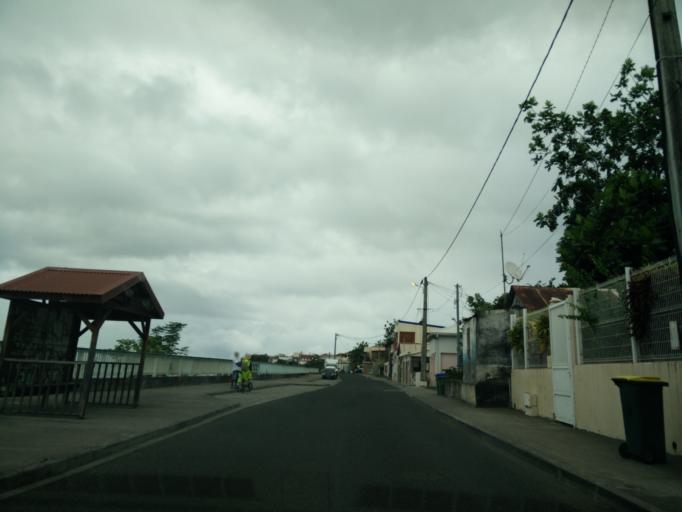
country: MQ
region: Martinique
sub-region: Martinique
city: Saint-Pierre
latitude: 14.7980
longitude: -61.2221
